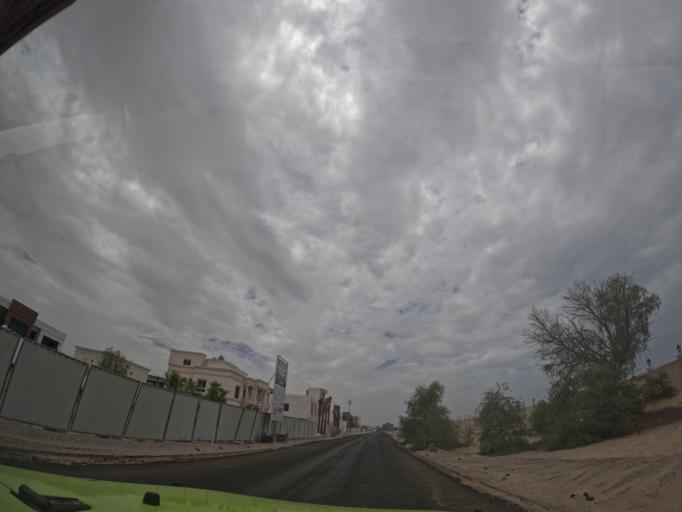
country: AE
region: Ash Shariqah
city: Sharjah
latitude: 25.1526
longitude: 55.3726
